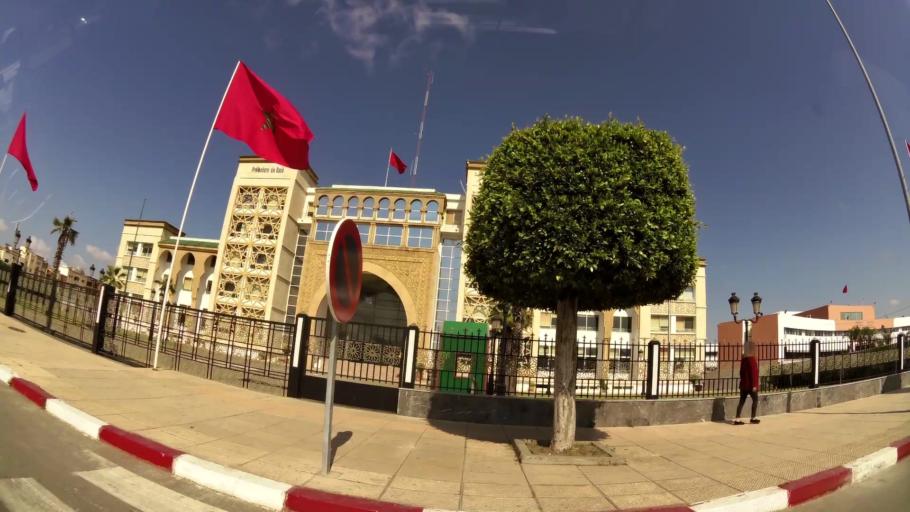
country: MA
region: Rabat-Sale-Zemmour-Zaer
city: Sale
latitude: 34.0386
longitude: -6.7856
